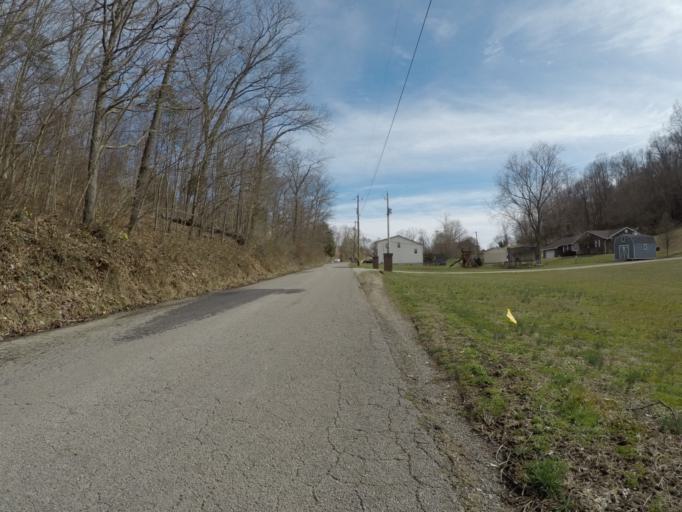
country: US
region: Ohio
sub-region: Lawrence County
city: Burlington
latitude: 38.3483
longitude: -82.5085
